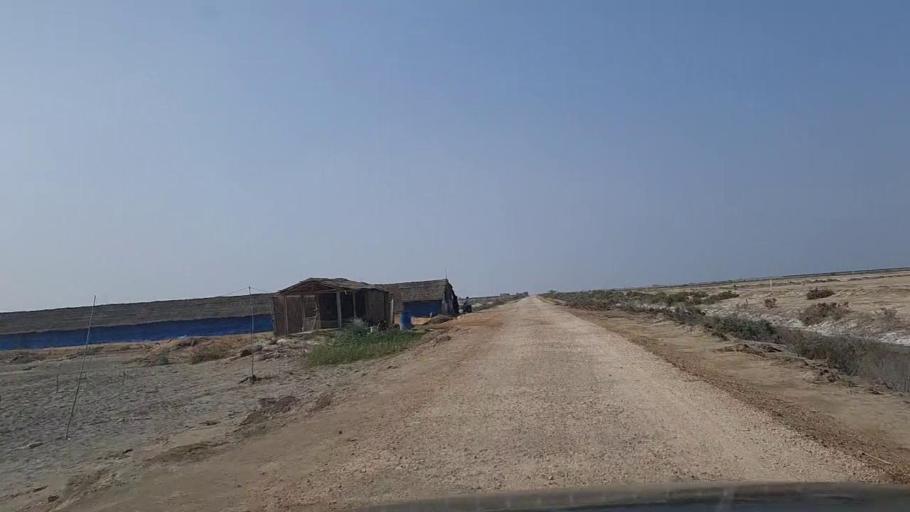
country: PK
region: Sindh
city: Gharo
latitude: 24.7074
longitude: 67.5414
